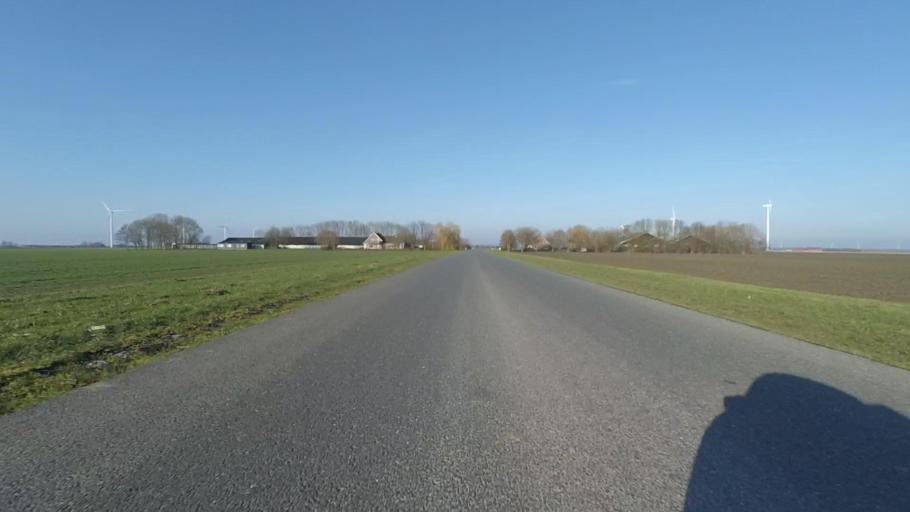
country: NL
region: Utrecht
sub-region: Gemeente Bunschoten
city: Spakenburg
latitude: 52.2915
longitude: 5.3942
